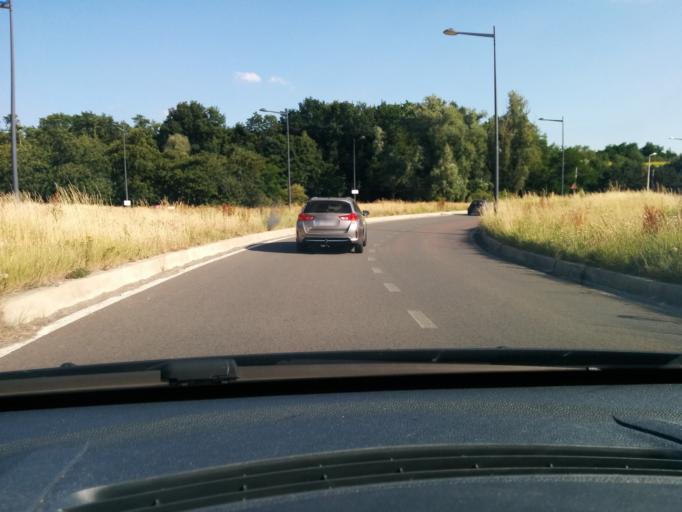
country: BE
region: Flanders
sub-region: Provincie Oost-Vlaanderen
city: Gent
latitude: 51.0271
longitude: 3.6963
